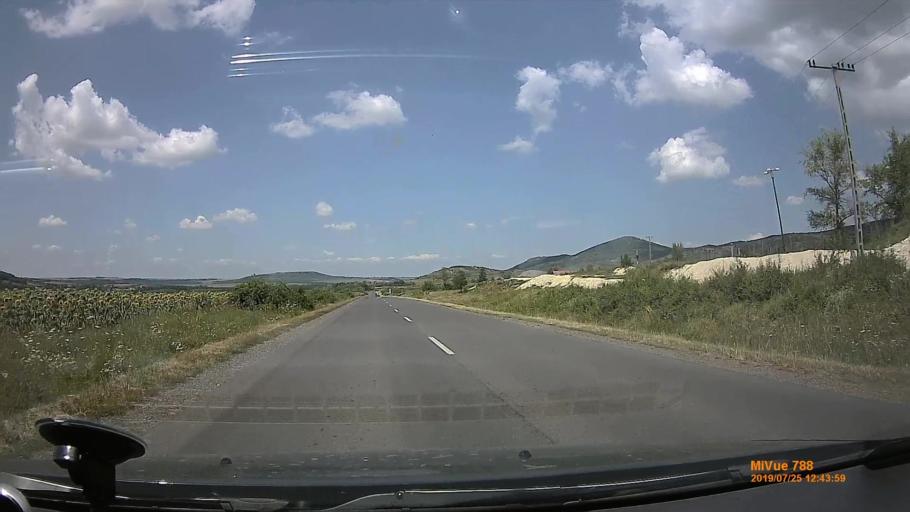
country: HU
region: Borsod-Abauj-Zemplen
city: Tallya
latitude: 48.2287
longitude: 21.2193
